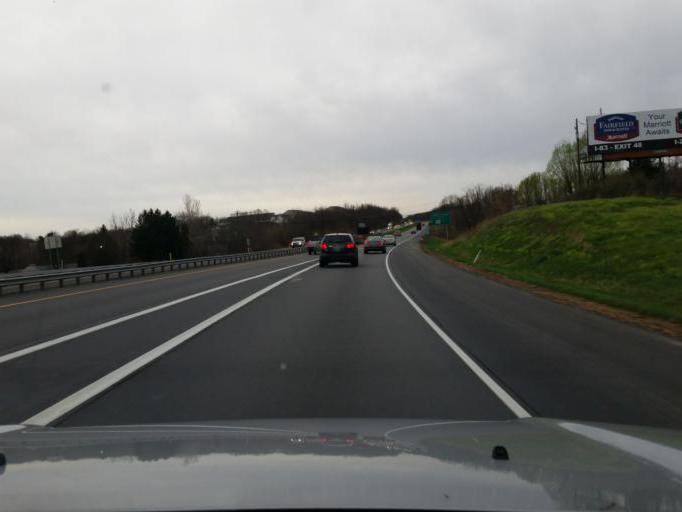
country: US
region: Pennsylvania
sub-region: Dauphin County
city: Highspire
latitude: 40.2243
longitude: -76.7911
